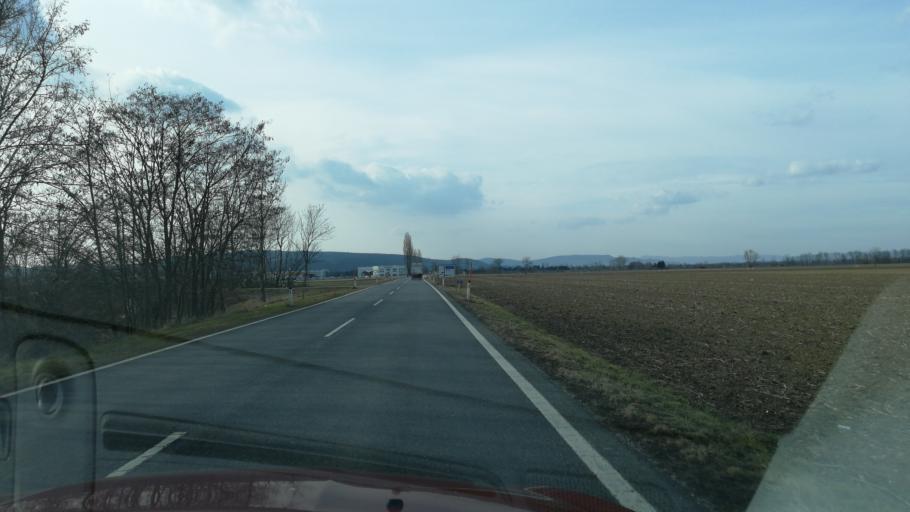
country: AT
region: Lower Austria
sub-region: Politischer Bezirk Tulln
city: Grafenworth
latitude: 48.3352
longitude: 15.8316
